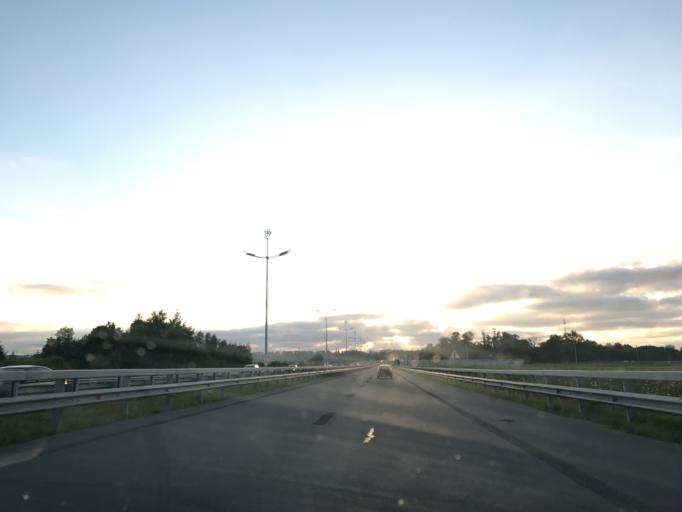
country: RU
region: Kaliningrad
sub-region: Gorod Kaliningrad
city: Pionerskiy
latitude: 54.9149
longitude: 20.1977
